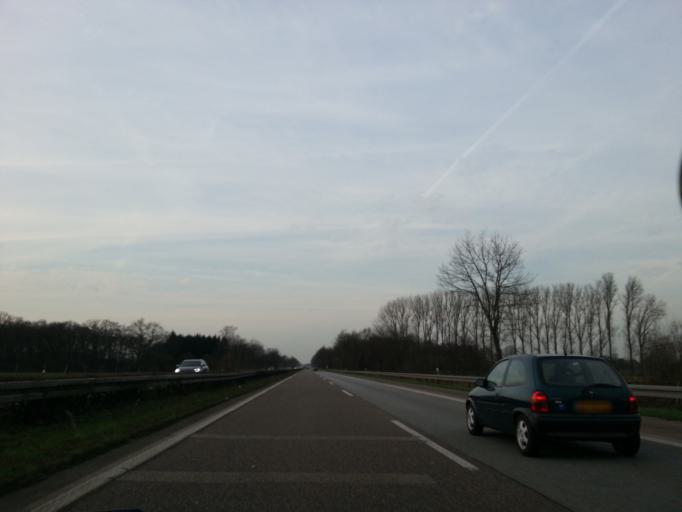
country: DE
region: North Rhine-Westphalia
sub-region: Regierungsbezirk Munster
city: Isselburg
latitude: 51.8077
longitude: 6.4700
